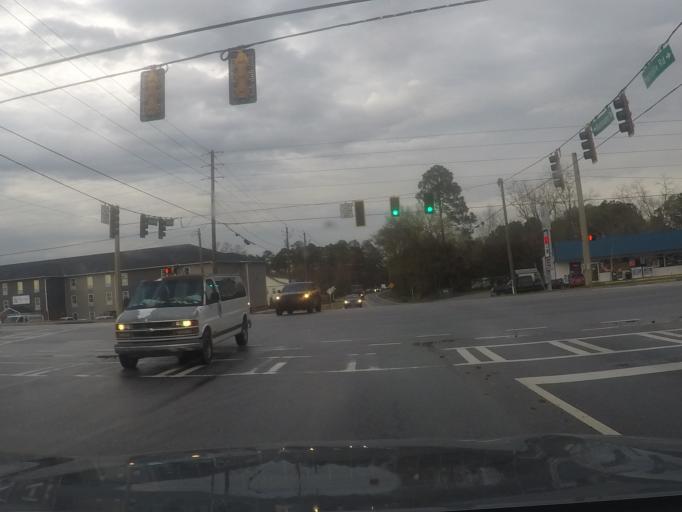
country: US
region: Georgia
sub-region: Bulloch County
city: Statesboro
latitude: 32.3974
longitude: -81.7566
